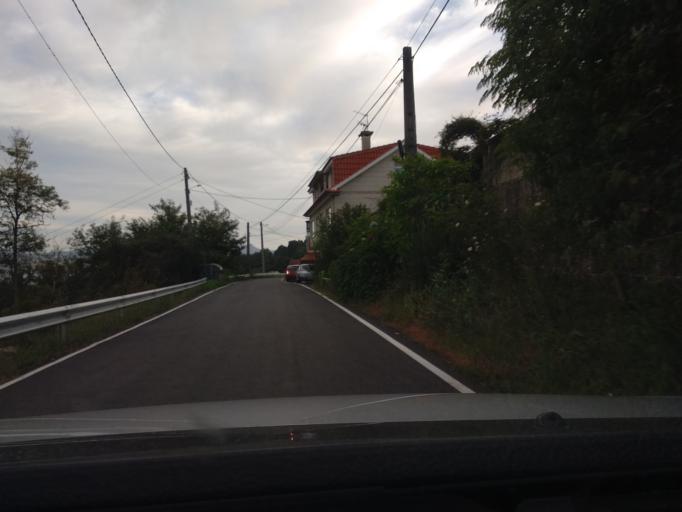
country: ES
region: Galicia
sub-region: Provincia de Pontevedra
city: Moana
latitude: 42.2949
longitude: -8.7385
